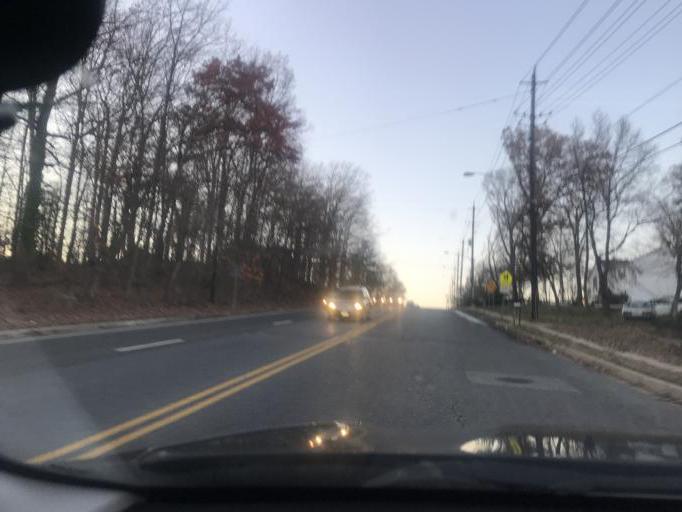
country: US
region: Maryland
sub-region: Prince George's County
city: Oxon Hill
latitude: 38.7965
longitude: -76.9768
